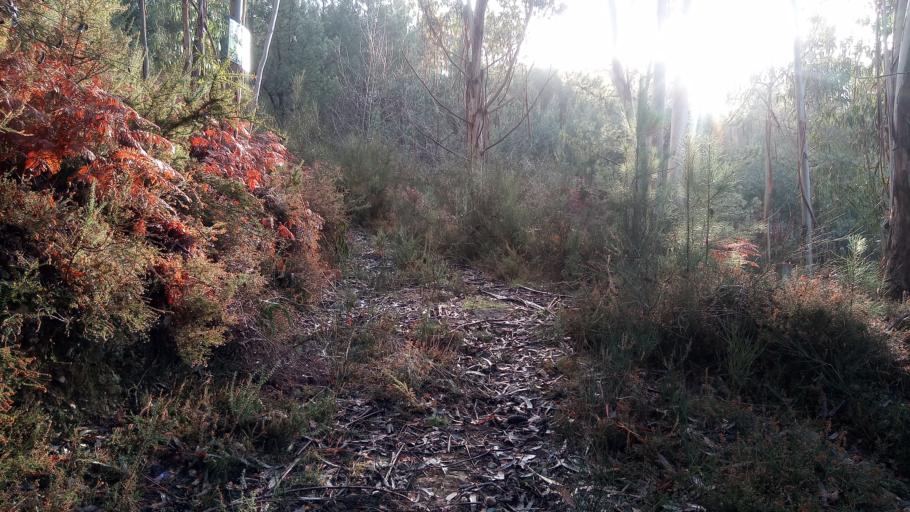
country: PT
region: Viana do Castelo
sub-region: Paredes de Coura
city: Paredes de Coura
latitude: 41.8953
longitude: -8.6130
